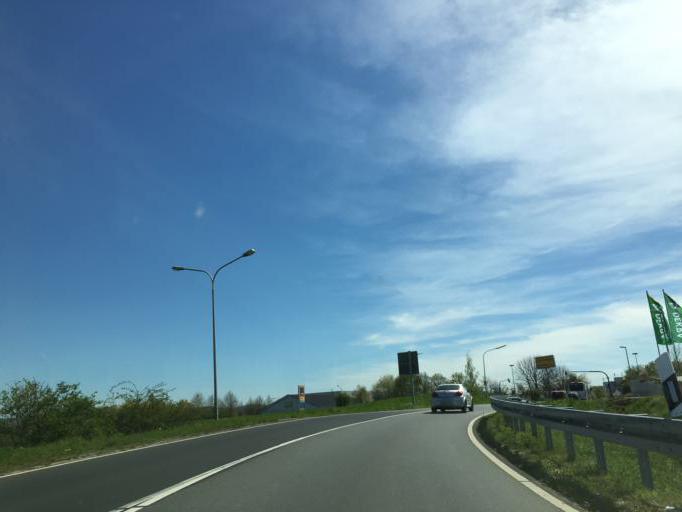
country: DE
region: Hesse
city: Reinheim
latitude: 49.8376
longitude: 8.8319
